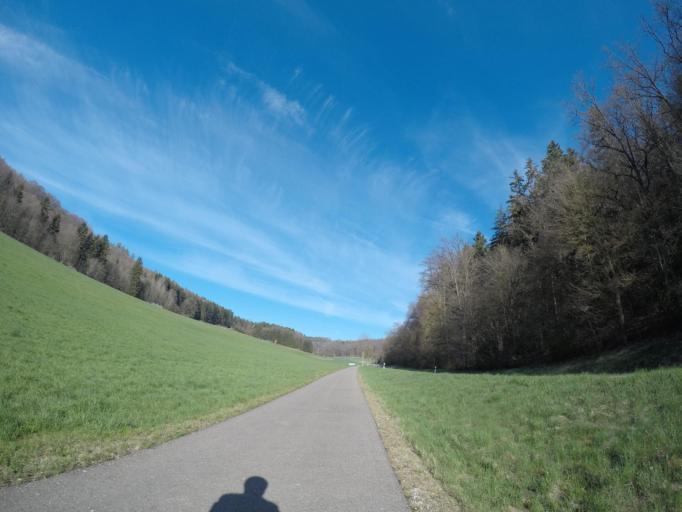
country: DE
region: Baden-Wuerttemberg
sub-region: Tuebingen Region
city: Allmendingen
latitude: 48.3452
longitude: 9.6971
